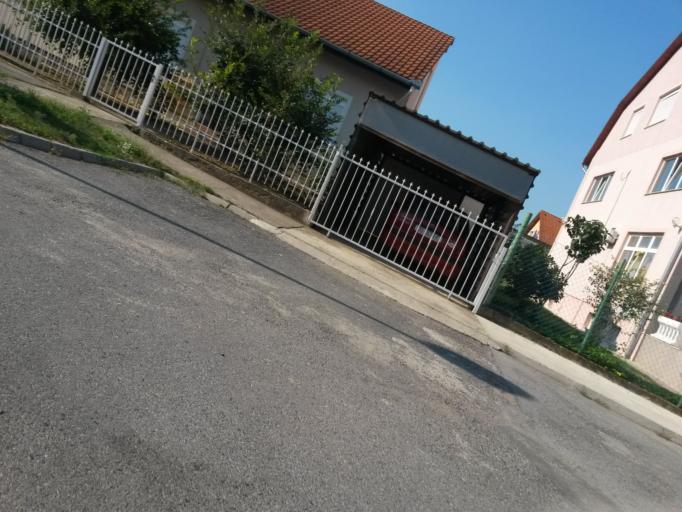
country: HR
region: Osjecko-Baranjska
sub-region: Grad Osijek
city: Osijek
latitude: 45.5425
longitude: 18.7049
